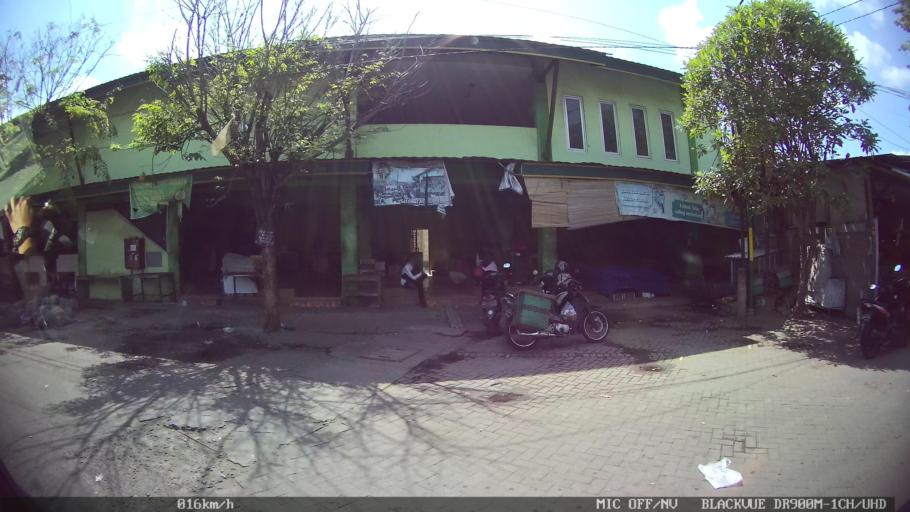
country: ID
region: Daerah Istimewa Yogyakarta
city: Sewon
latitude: -7.8335
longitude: 110.3884
